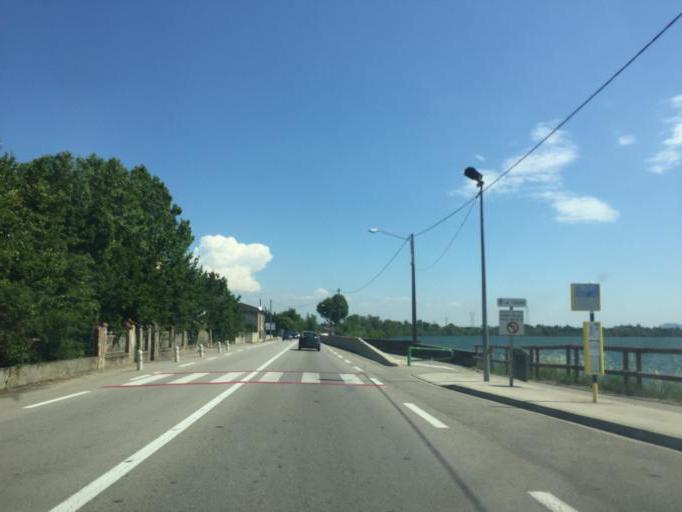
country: FR
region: Rhone-Alpes
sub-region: Departement de l'Ardeche
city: Tournon-sur-Rhone
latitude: 45.0626
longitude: 4.8589
